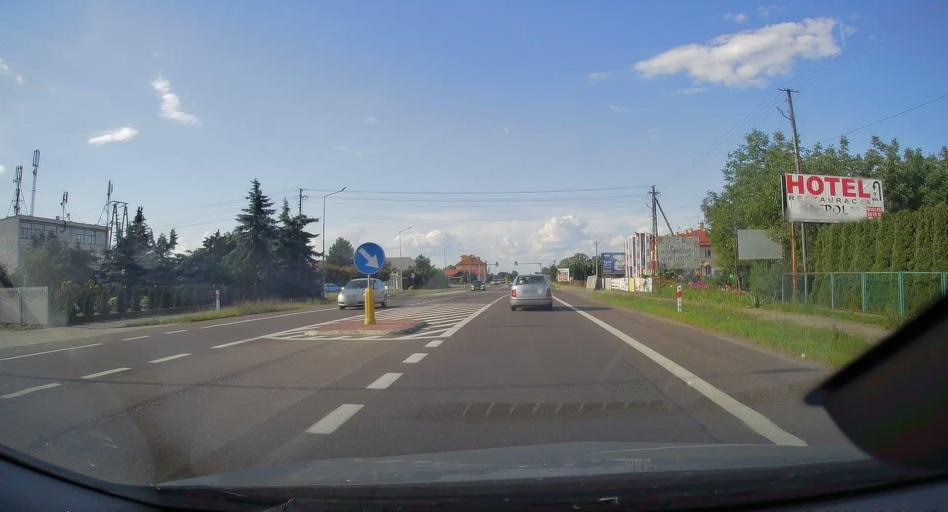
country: PL
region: Subcarpathian Voivodeship
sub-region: Powiat przemyski
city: Orly
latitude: 49.8725
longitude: 22.8116
